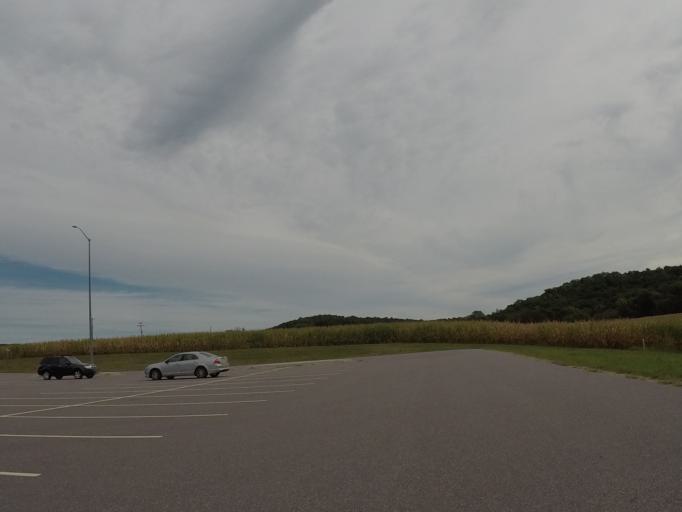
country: US
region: Wisconsin
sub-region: Sauk County
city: Sauk City
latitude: 43.2627
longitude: -89.7105
